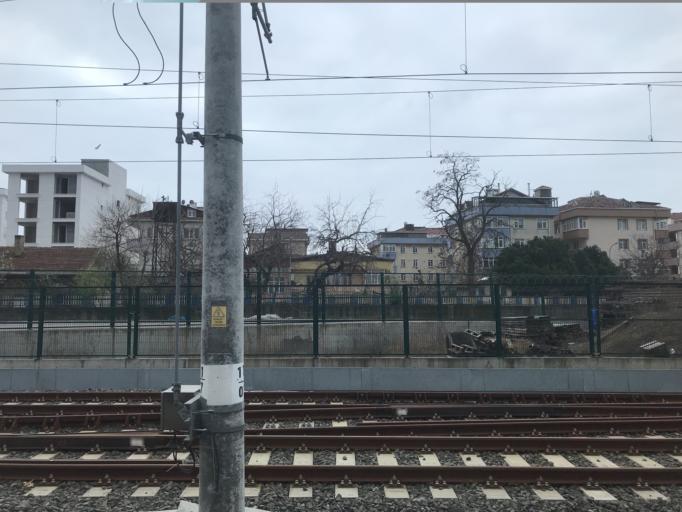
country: TR
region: Istanbul
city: Icmeler
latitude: 40.8293
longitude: 29.3228
